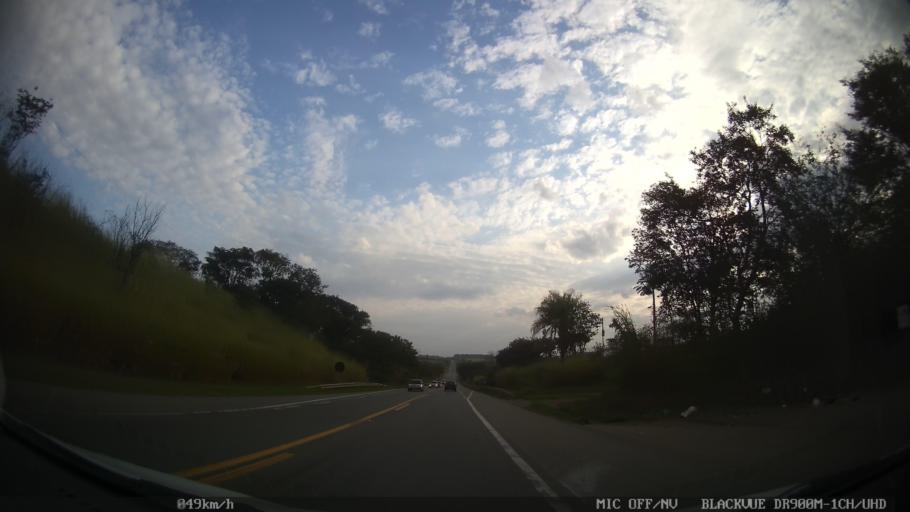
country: BR
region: Sao Paulo
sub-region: Cosmopolis
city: Cosmopolis
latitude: -22.6288
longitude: -47.2780
